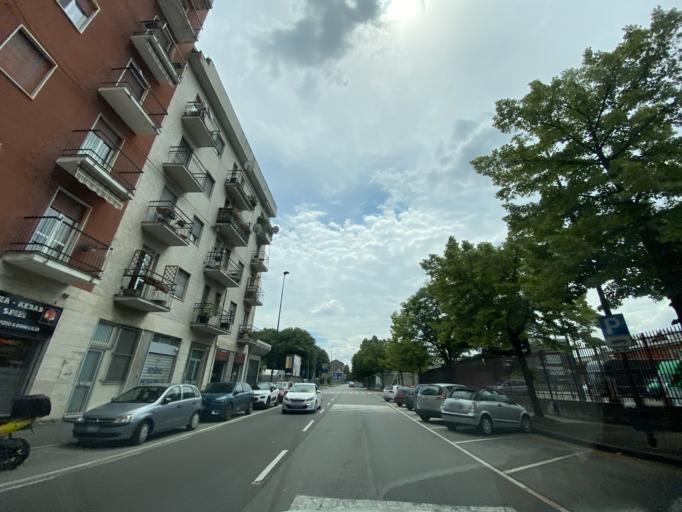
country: IT
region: Lombardy
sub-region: Citta metropolitana di Milano
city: Sesto San Giovanni
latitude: 45.5270
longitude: 9.2409
